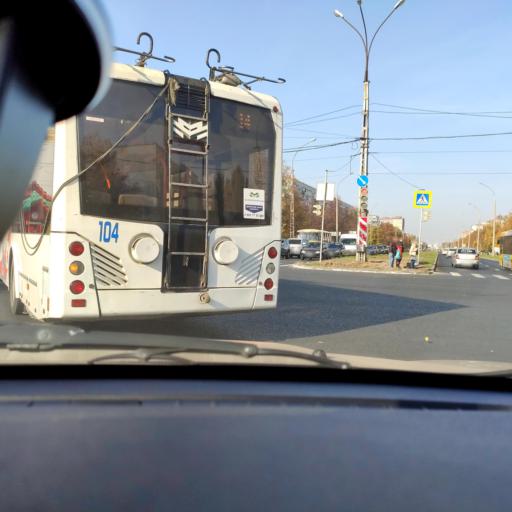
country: RU
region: Samara
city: Tol'yatti
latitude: 53.5335
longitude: 49.3287
